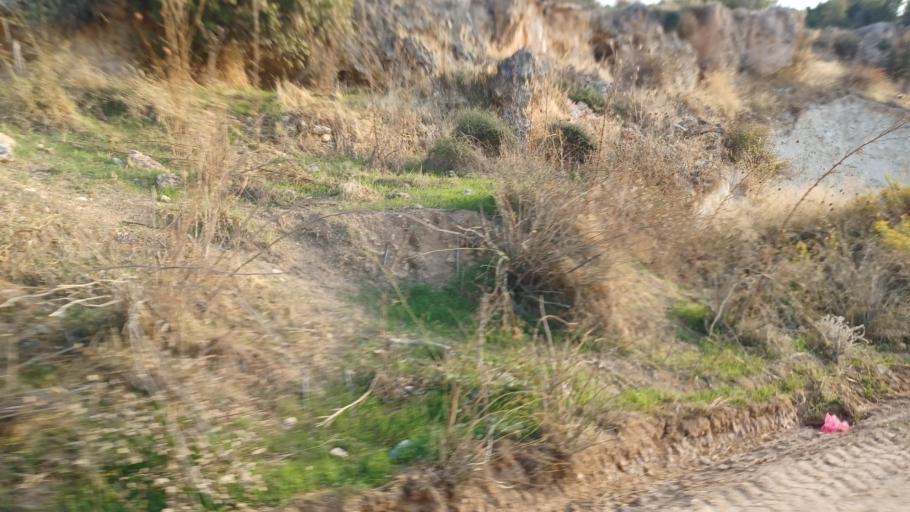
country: CY
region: Pafos
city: Polis
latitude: 34.9627
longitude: 32.4876
